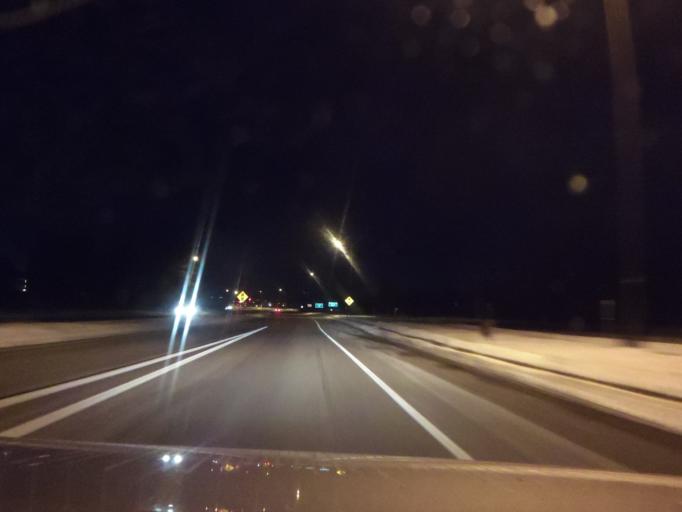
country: US
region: Minnesota
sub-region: Dakota County
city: Mendota Heights
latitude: 44.9022
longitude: -93.1989
